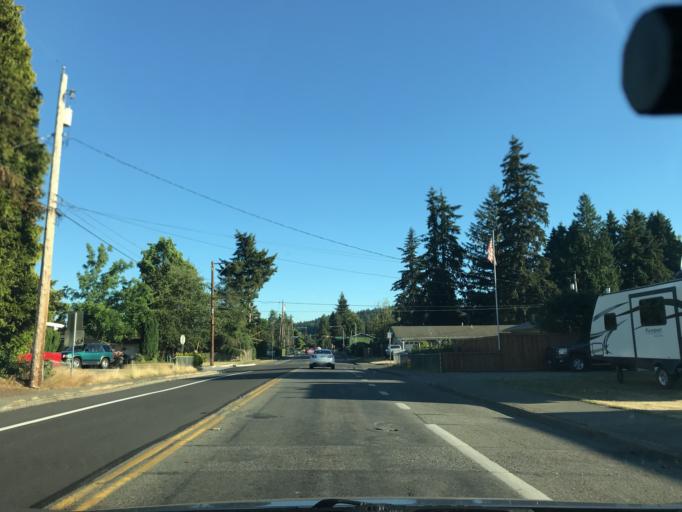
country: US
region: Washington
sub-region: King County
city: Auburn
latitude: 47.2848
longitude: -122.2080
